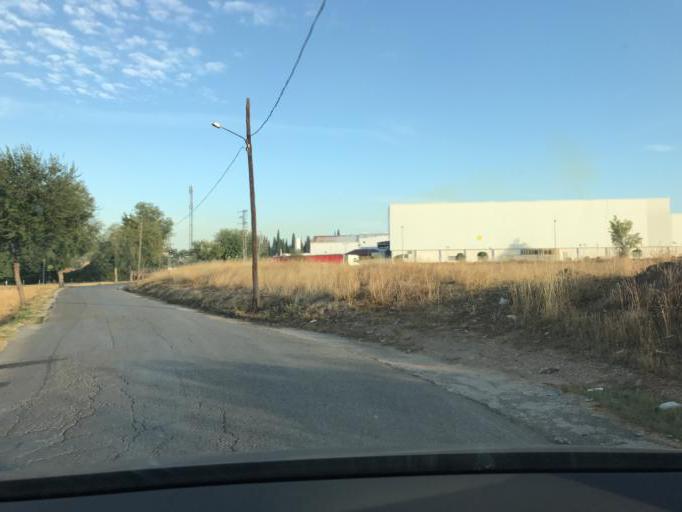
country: ES
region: Andalusia
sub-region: Provincia de Granada
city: Pulianas
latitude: 37.2274
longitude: -3.6106
